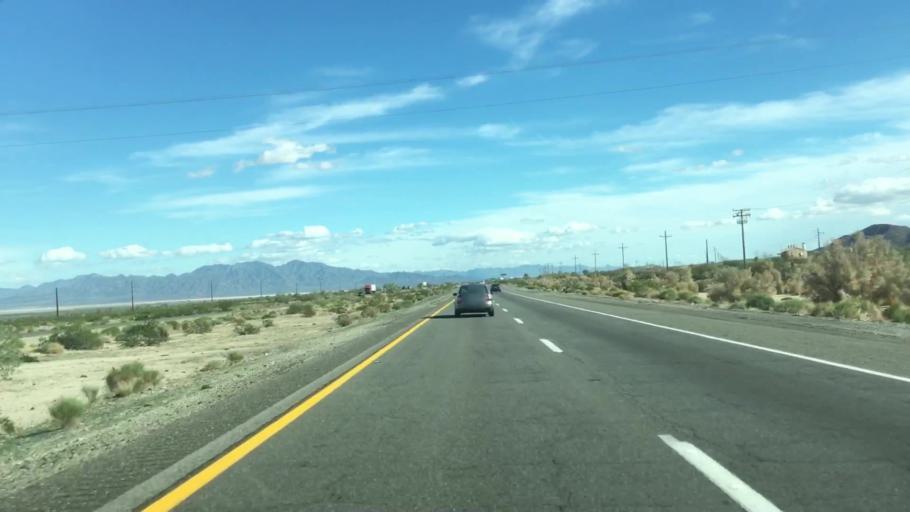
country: US
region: California
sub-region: Imperial County
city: Niland
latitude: 33.7105
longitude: -115.3877
